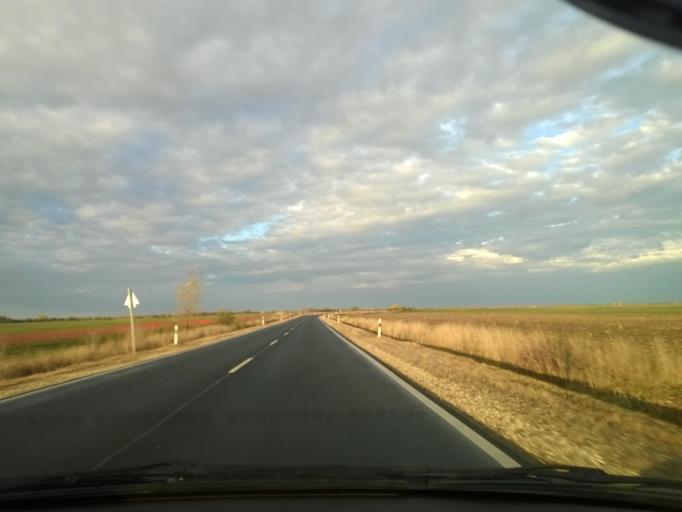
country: HU
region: Bacs-Kiskun
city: Dunapataj
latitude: 46.5960
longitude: 18.9792
